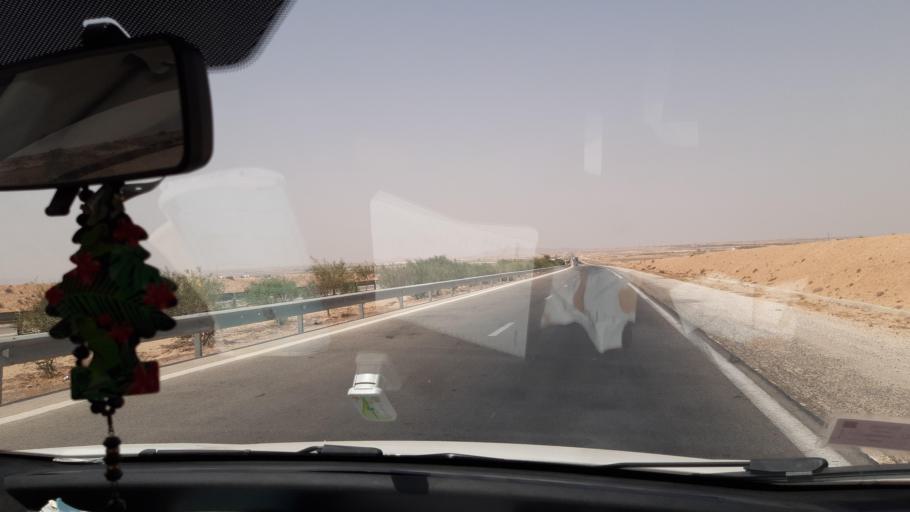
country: TN
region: Qabis
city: Gabes
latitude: 33.9609
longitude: 9.9553
